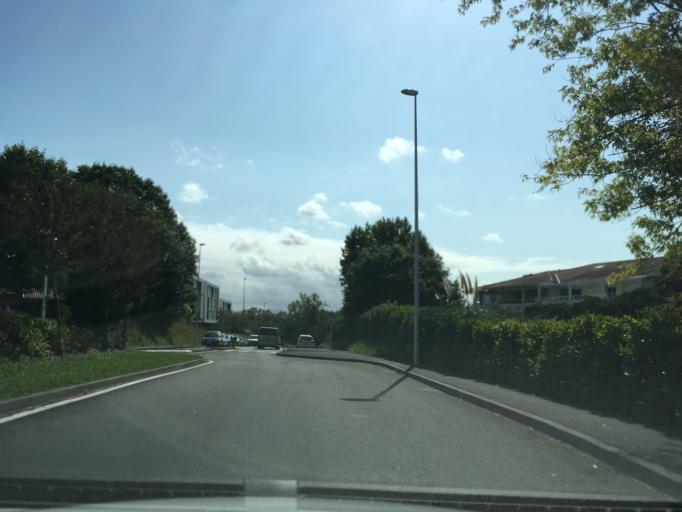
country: FR
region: Aquitaine
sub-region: Departement des Pyrenees-Atlantiques
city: Bayonne
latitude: 43.4803
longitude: -1.4891
